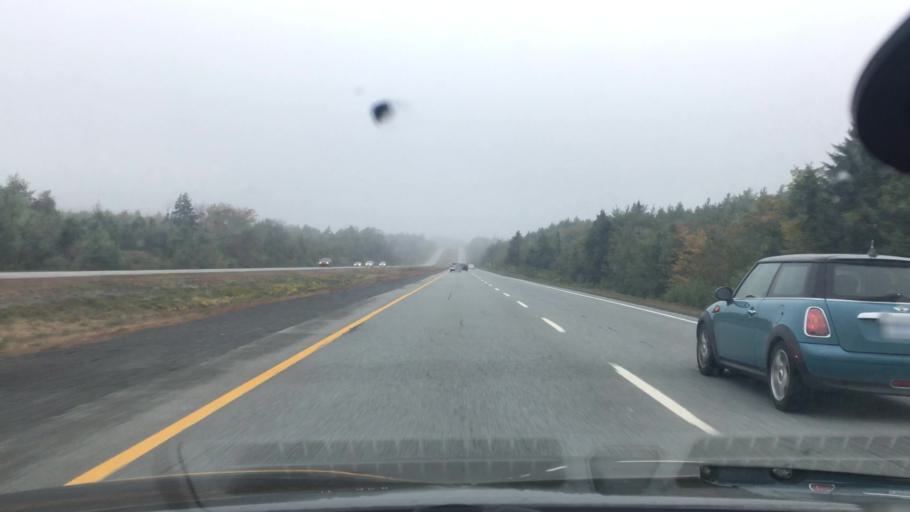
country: CA
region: Nova Scotia
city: Windsor
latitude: 44.8785
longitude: -63.8542
